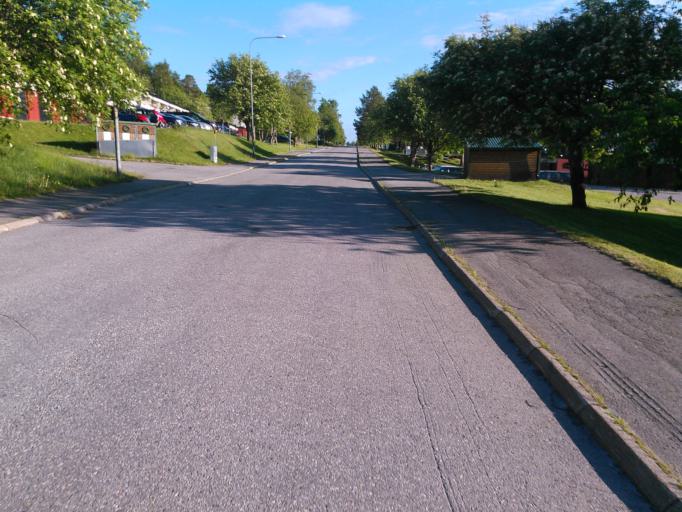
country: SE
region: Vaesterbotten
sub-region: Umea Kommun
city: Ersmark
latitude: 63.8429
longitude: 20.3240
